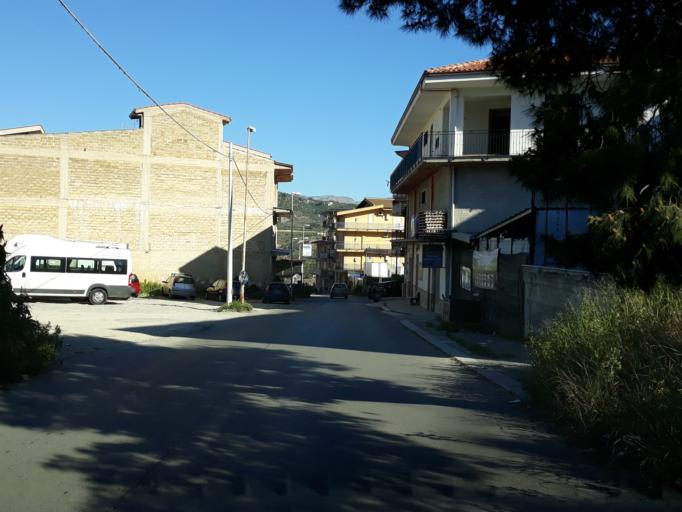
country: IT
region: Sicily
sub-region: Palermo
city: Misilmeri
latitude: 38.0281
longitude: 13.4510
